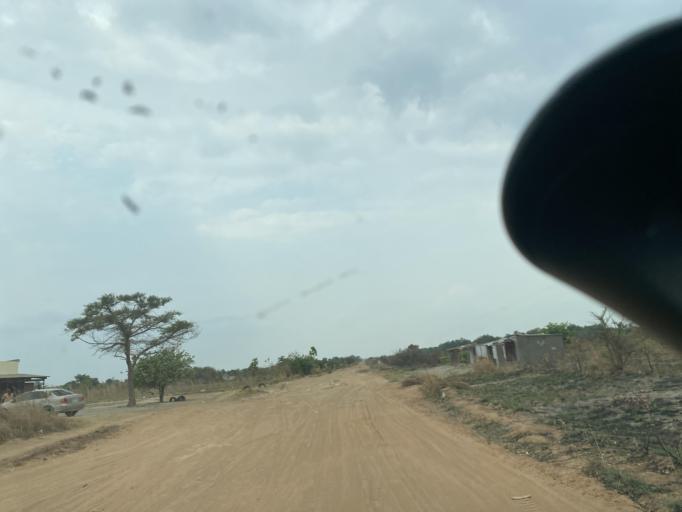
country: ZM
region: Lusaka
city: Lusaka
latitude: -15.2115
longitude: 28.3393
